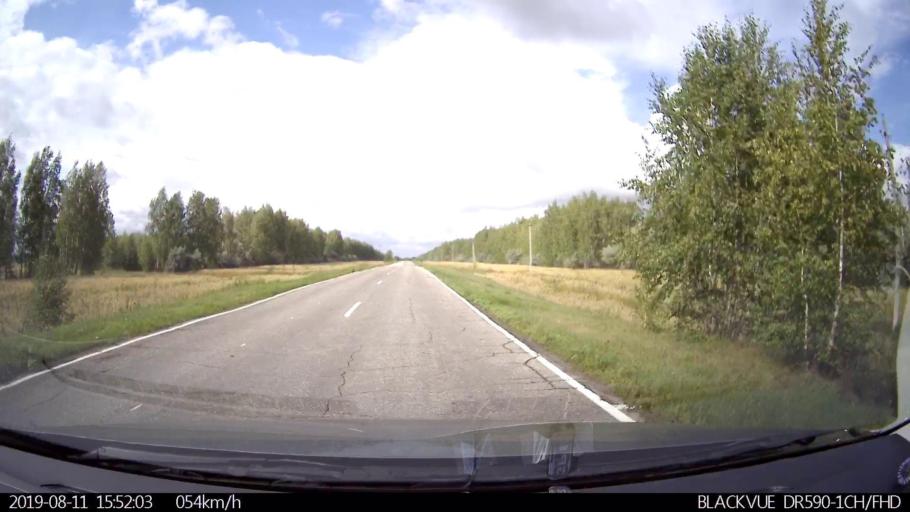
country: RU
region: Ulyanovsk
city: Ignatovka
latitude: 53.9236
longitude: 47.6562
